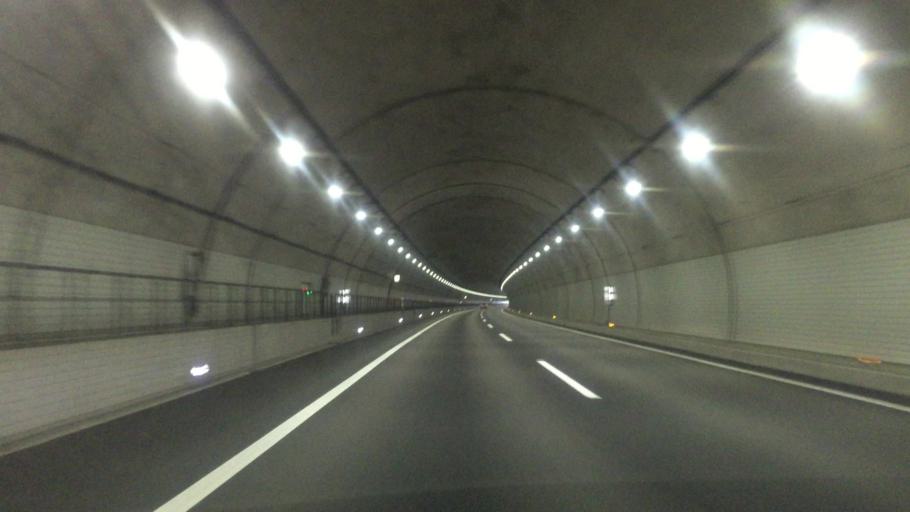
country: JP
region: Aichi
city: Okazaki
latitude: 34.9497
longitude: 137.2551
